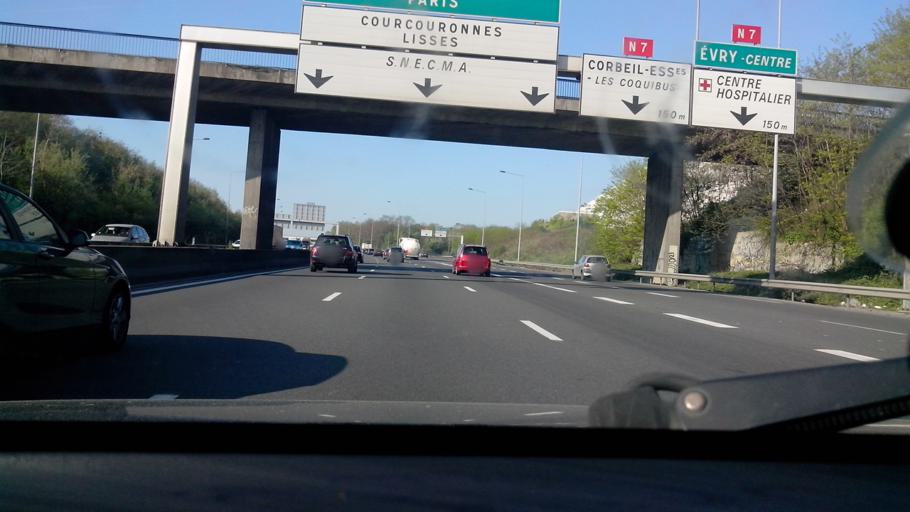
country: FR
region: Ile-de-France
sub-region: Departement de l'Essonne
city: Evry
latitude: 48.6211
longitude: 2.4615
